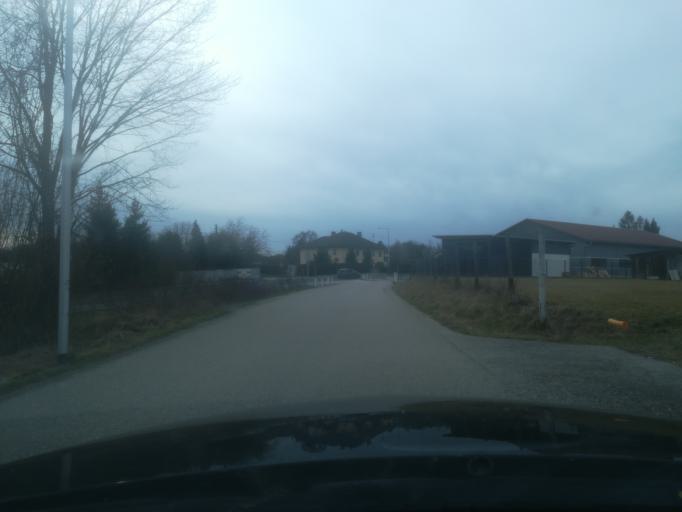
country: AT
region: Upper Austria
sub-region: Wels-Land
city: Bad Wimsbach-Neydharting
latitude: 48.0922
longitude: 13.9104
